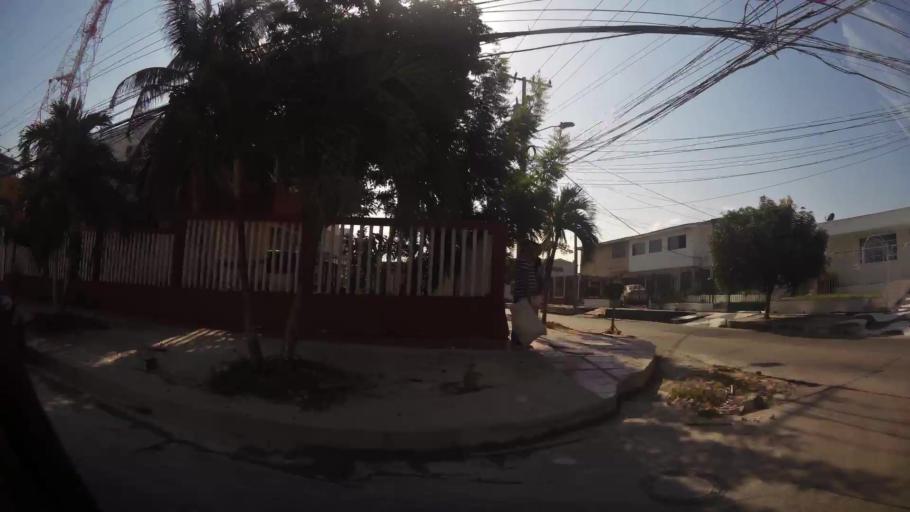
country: CO
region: Atlantico
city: Barranquilla
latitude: 10.9952
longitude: -74.8276
